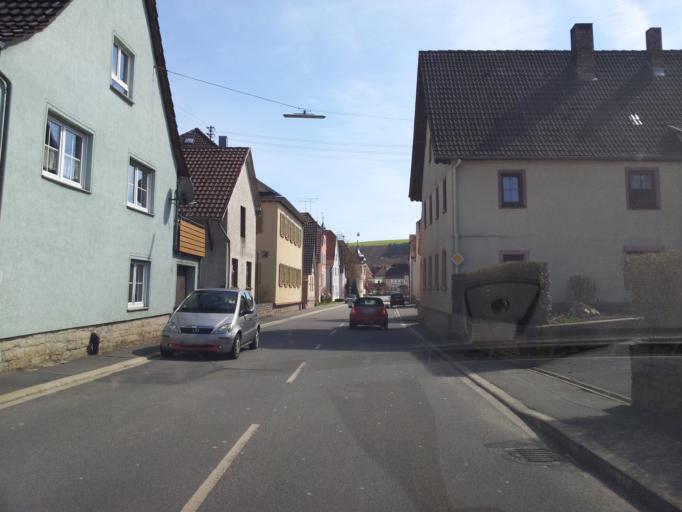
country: DE
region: Baden-Wuerttemberg
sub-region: Regierungsbezirk Stuttgart
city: Lauda-Konigshofen
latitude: 49.5157
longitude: 9.6868
